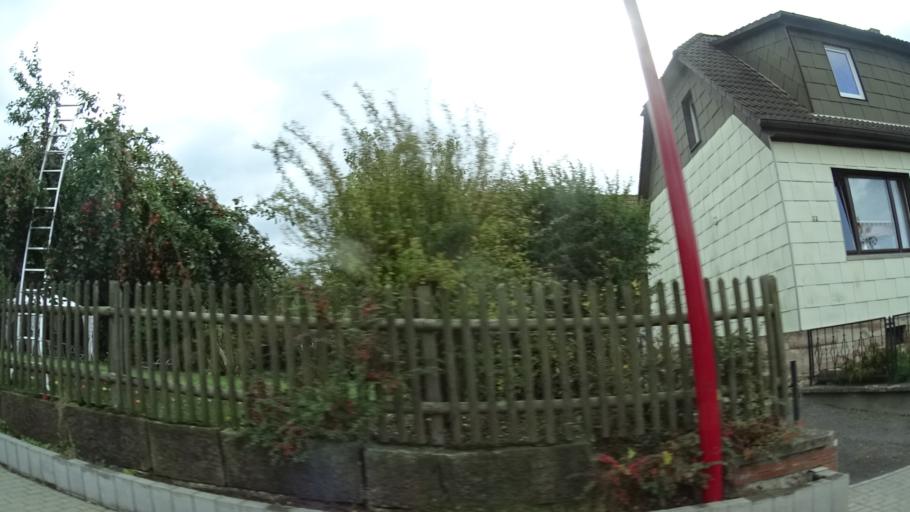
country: DE
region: Thuringia
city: Breitenbach
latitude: 50.7246
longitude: 10.4829
